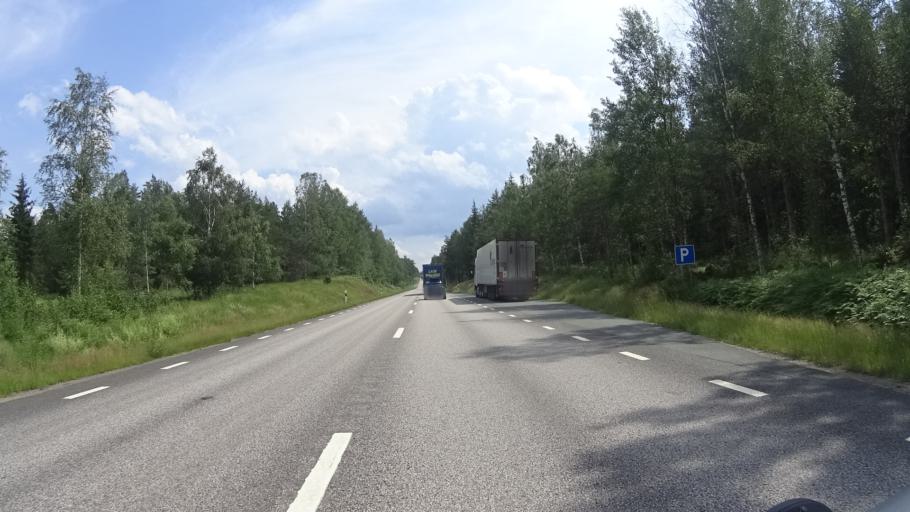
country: SE
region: Kalmar
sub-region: Hultsfreds Kommun
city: Hultsfred
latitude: 57.4855
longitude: 15.8294
